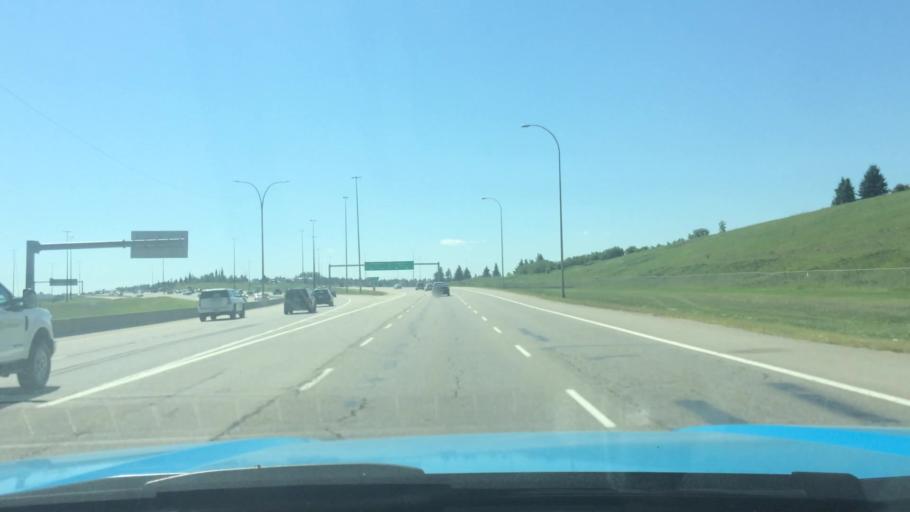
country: CA
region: Alberta
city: Calgary
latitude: 50.9580
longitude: -114.0301
